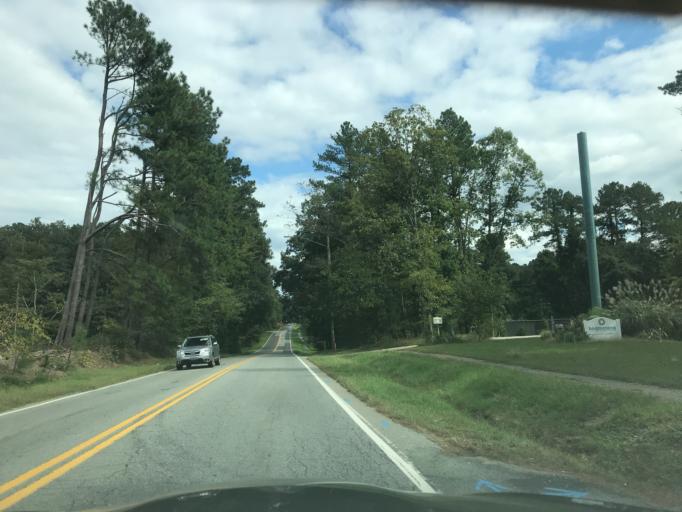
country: US
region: North Carolina
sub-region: Orange County
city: Chapel Hill
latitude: 35.9352
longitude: -79.0538
